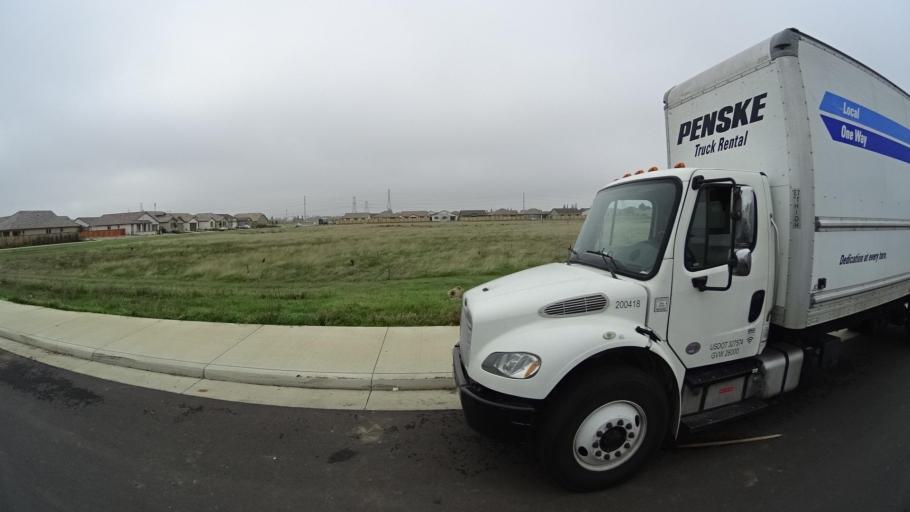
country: US
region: California
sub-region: Sacramento County
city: Elk Grove
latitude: 38.3984
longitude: -121.3441
